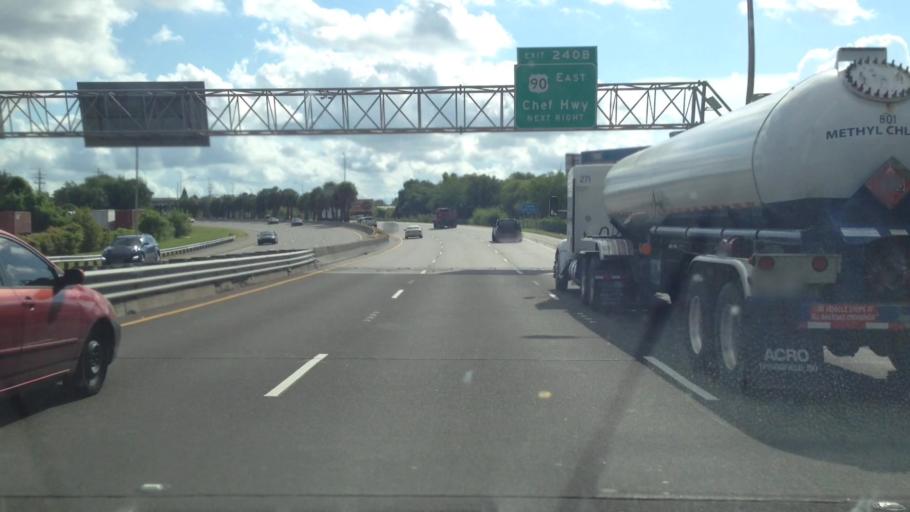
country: US
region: Louisiana
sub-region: Saint Bernard Parish
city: Arabi
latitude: 30.0068
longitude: -90.0172
